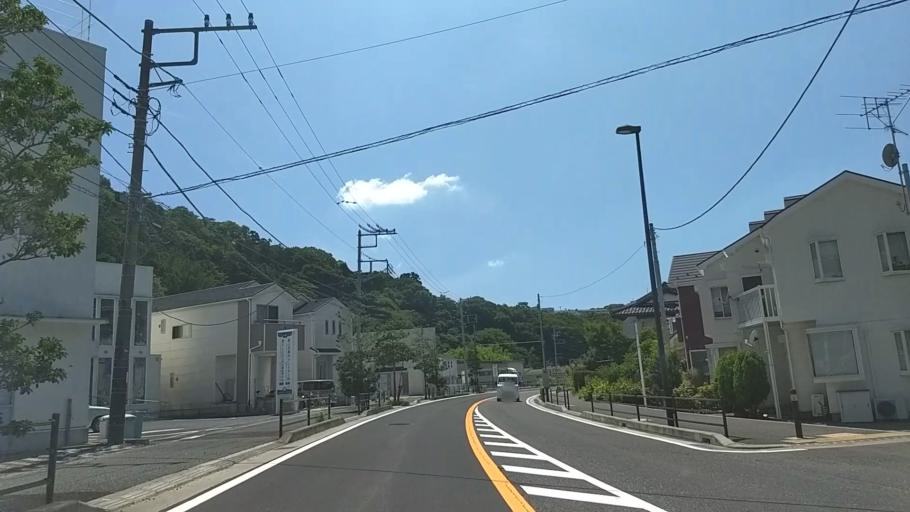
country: JP
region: Kanagawa
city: Hayama
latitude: 35.2832
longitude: 139.5884
